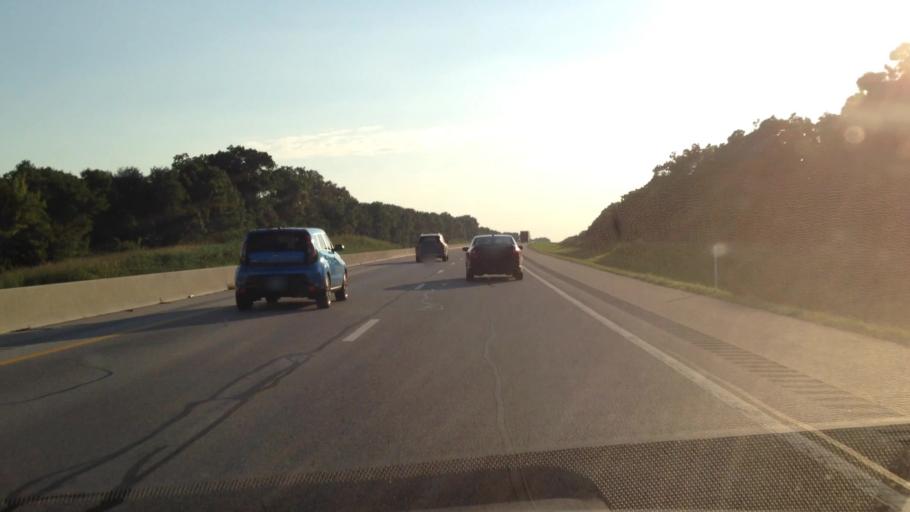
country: US
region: Kansas
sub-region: Cherokee County
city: Baxter Springs
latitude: 36.9403
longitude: -94.6920
